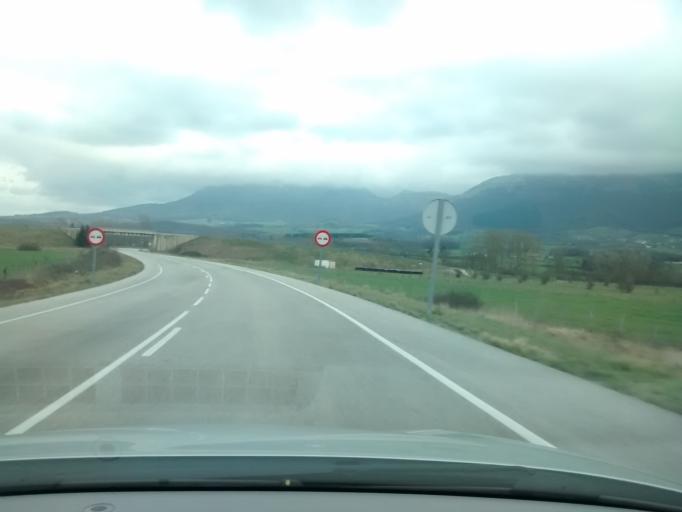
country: ES
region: Castille and Leon
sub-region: Provincia de Burgos
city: Villasana de Mena
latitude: 43.0945
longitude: -3.3035
